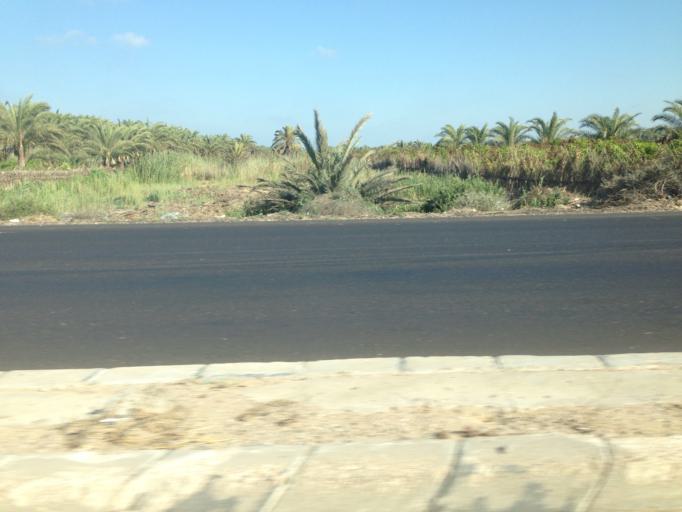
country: EG
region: Al Buhayrah
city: Idku
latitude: 31.3001
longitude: 30.2665
